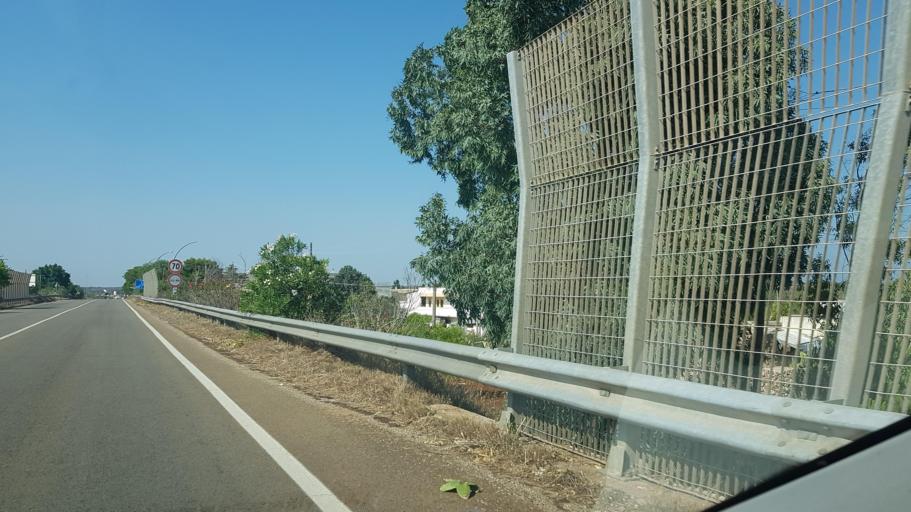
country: IT
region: Apulia
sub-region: Provincia di Lecce
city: Acquarica del Capo
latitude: 39.9148
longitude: 18.2338
